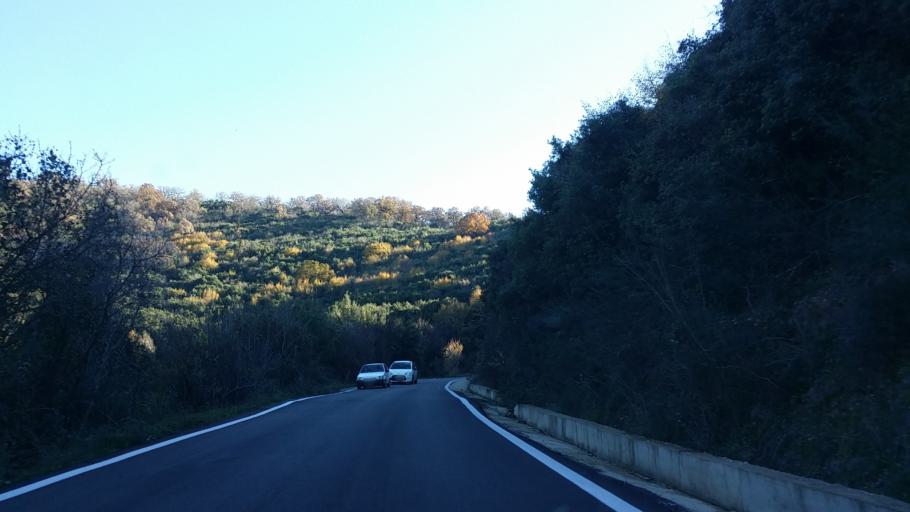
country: GR
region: West Greece
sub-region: Nomos Aitolias kai Akarnanias
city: Fitiai
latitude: 38.6417
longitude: 21.1894
